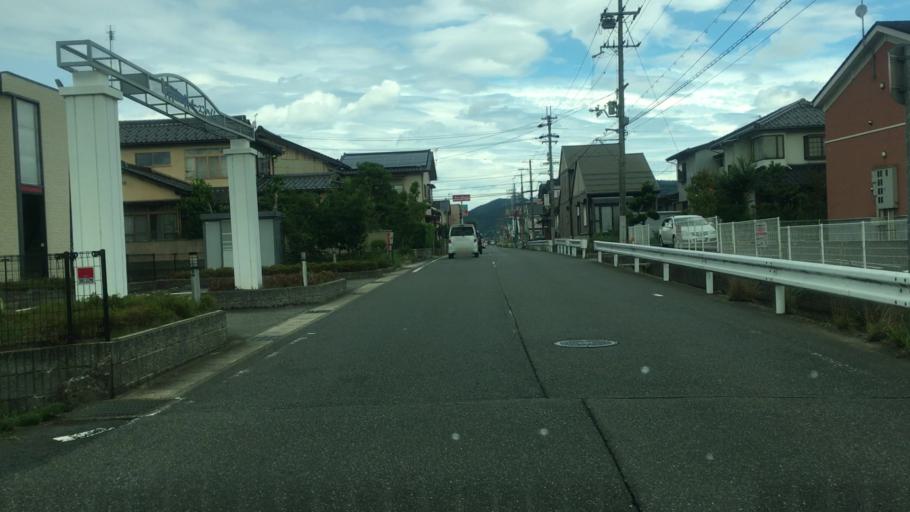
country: JP
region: Hyogo
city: Toyooka
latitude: 35.5508
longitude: 134.8130
